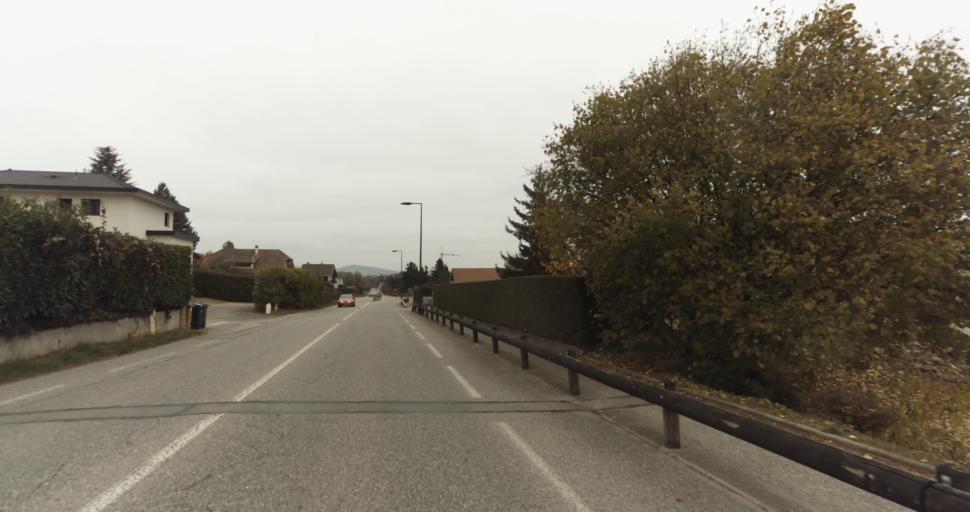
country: FR
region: Rhone-Alpes
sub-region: Departement de la Haute-Savoie
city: Poisy
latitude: 45.9154
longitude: 6.0544
